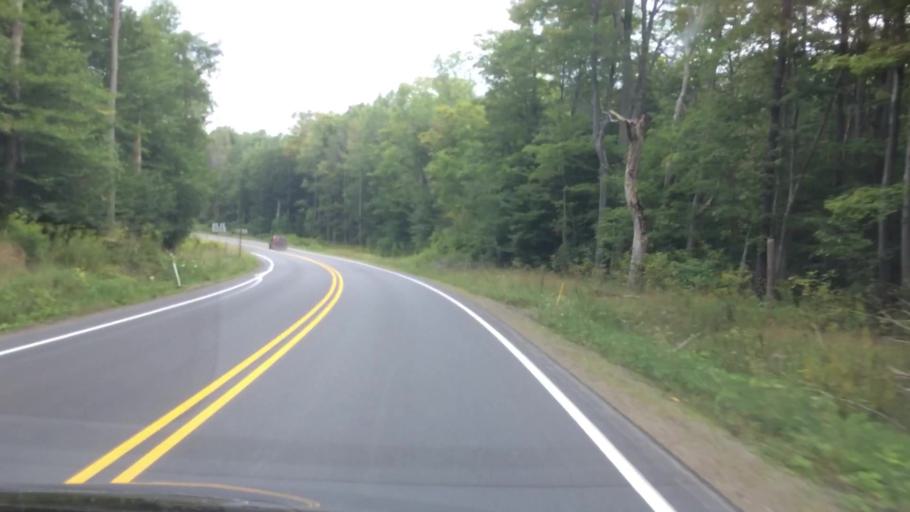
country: US
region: Pennsylvania
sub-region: McKean County
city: Bradford
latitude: 41.8800
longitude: -78.5769
